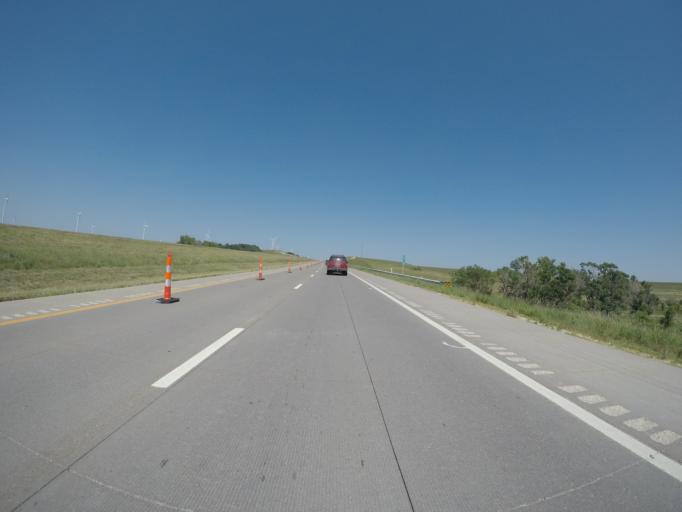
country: US
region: Kansas
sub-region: Lincoln County
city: Lincoln
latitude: 38.8692
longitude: -98.0662
